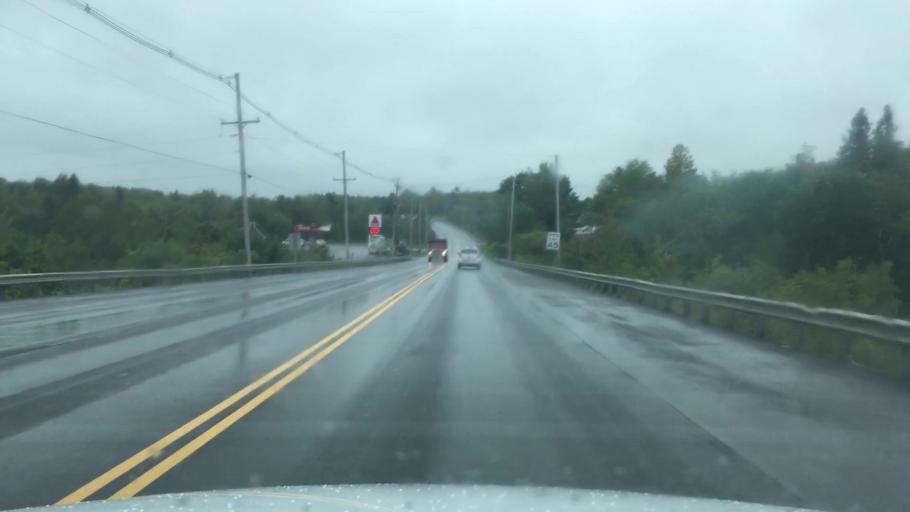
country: US
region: Maine
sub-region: Penobscot County
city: Hampden
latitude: 44.7714
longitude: -68.8577
